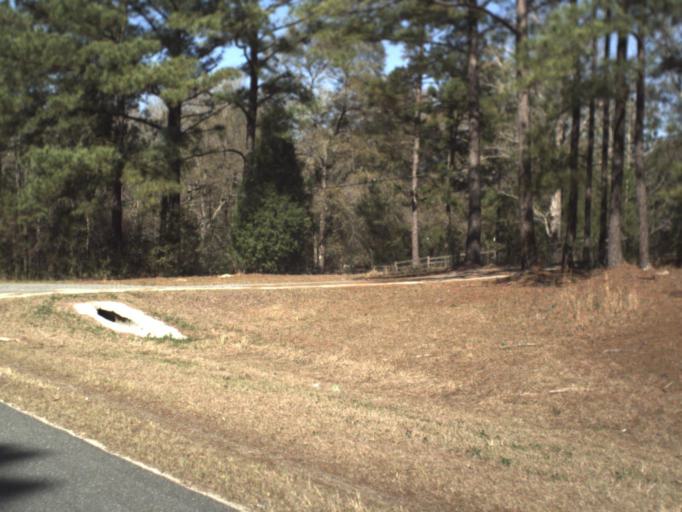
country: US
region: Florida
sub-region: Jackson County
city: Marianna
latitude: 30.7401
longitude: -85.1222
